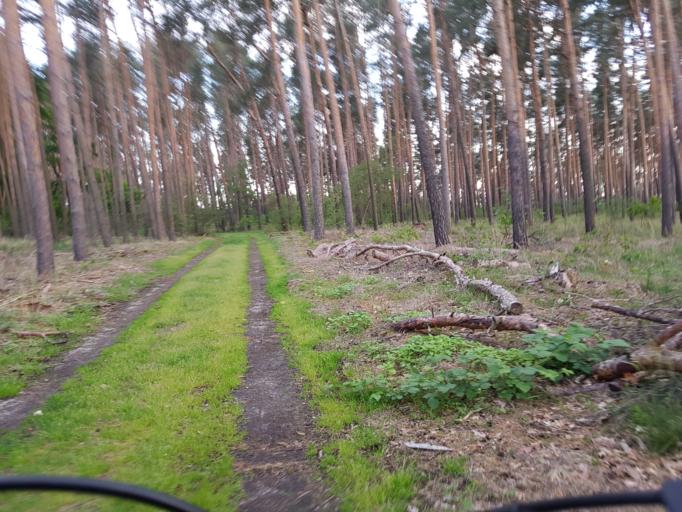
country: DE
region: Brandenburg
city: Bad Liebenwerda
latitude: 51.5547
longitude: 13.4117
